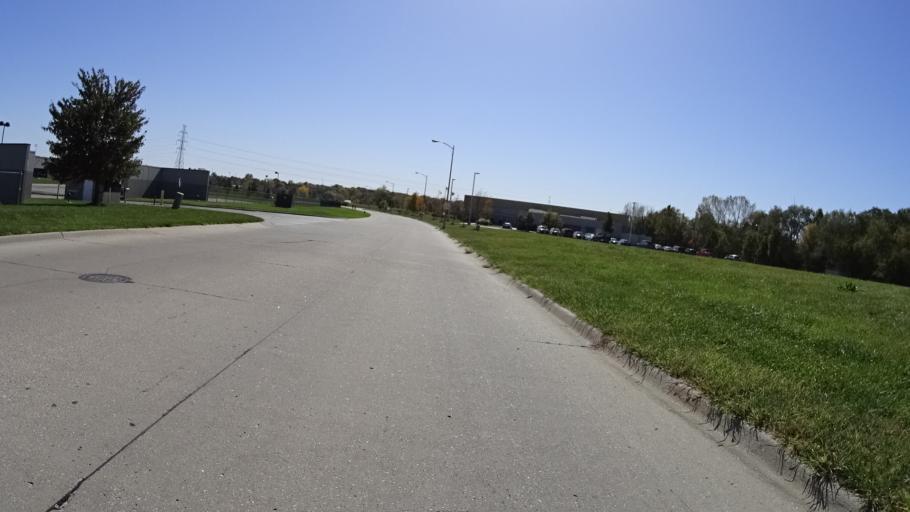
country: US
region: Nebraska
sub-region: Sarpy County
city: Papillion
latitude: 41.1582
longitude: -96.0320
